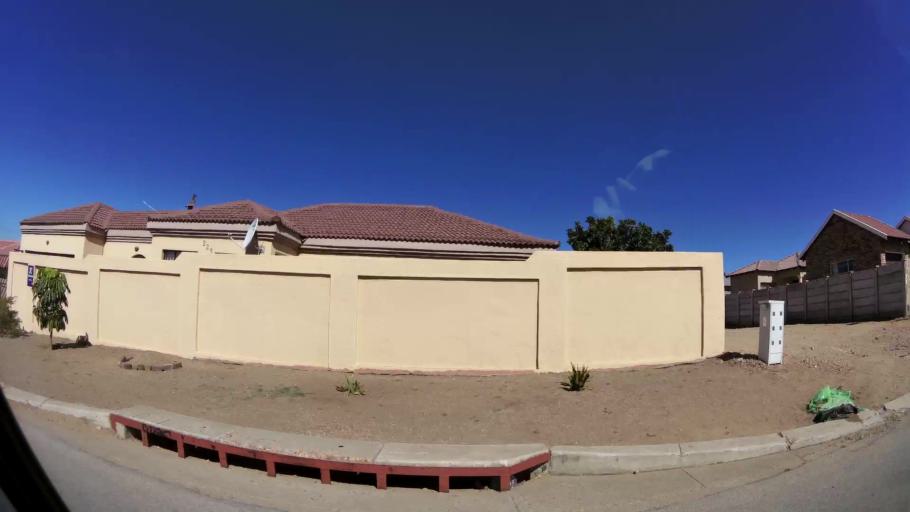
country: ZA
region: Limpopo
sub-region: Capricorn District Municipality
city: Polokwane
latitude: -23.8709
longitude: 29.4295
